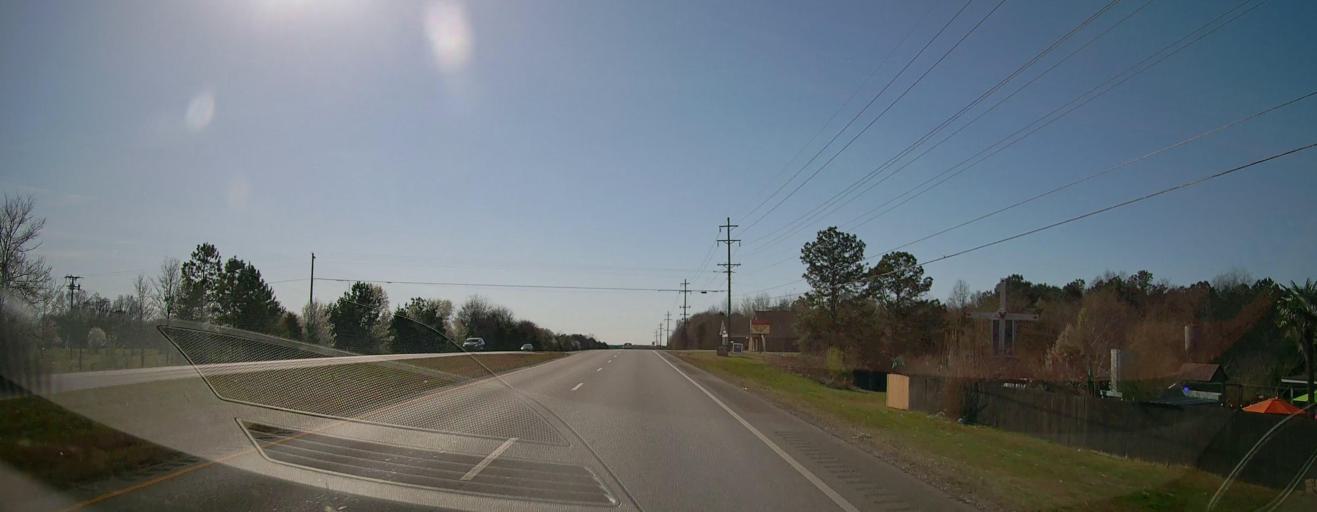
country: US
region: Alabama
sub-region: Lauderdale County
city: Killen
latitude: 34.8598
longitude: -87.4987
